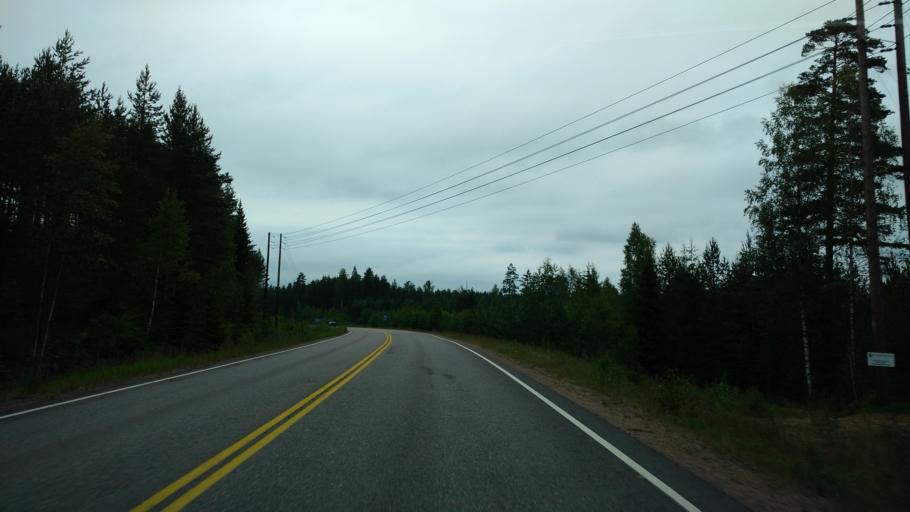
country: FI
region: Varsinais-Suomi
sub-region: Salo
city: Kiikala
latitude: 60.4245
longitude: 23.5934
